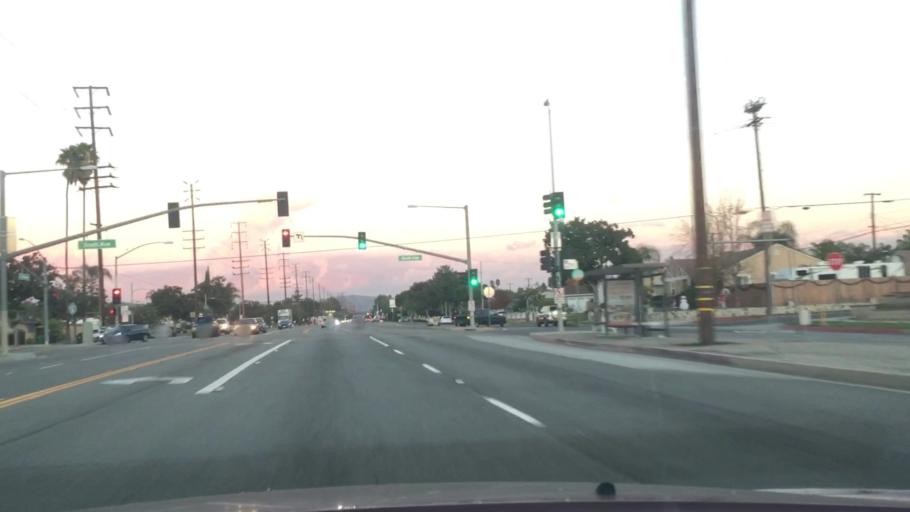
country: US
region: California
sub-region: Los Angeles County
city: East La Mirada
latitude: 33.9292
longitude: -118.0013
